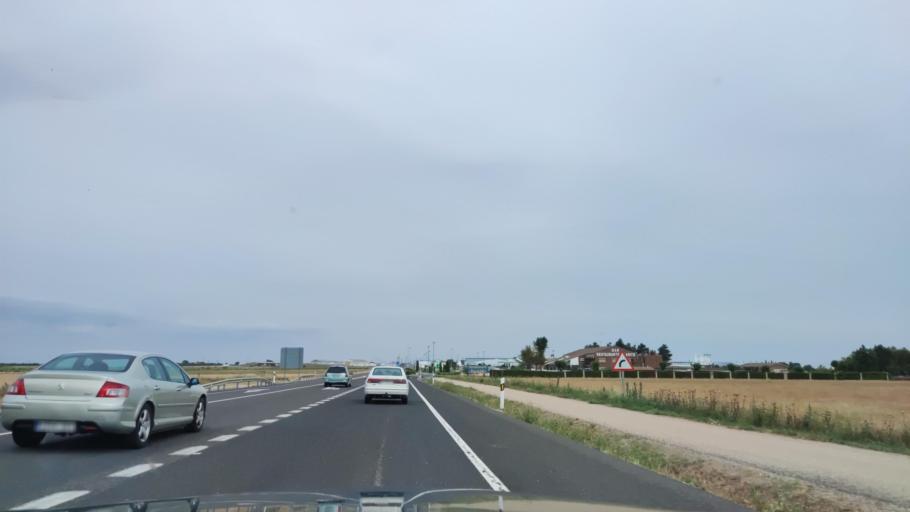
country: ES
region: Castille-La Mancha
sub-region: Provincia de Albacete
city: La Roda
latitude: 39.2192
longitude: -2.1884
